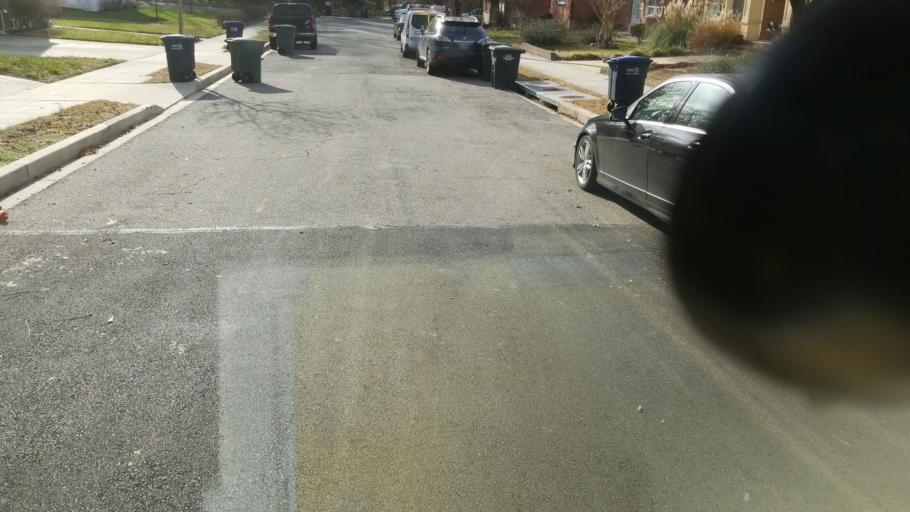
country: US
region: Maryland
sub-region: Prince George's County
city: Silver Hill
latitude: 38.8753
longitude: -76.9588
